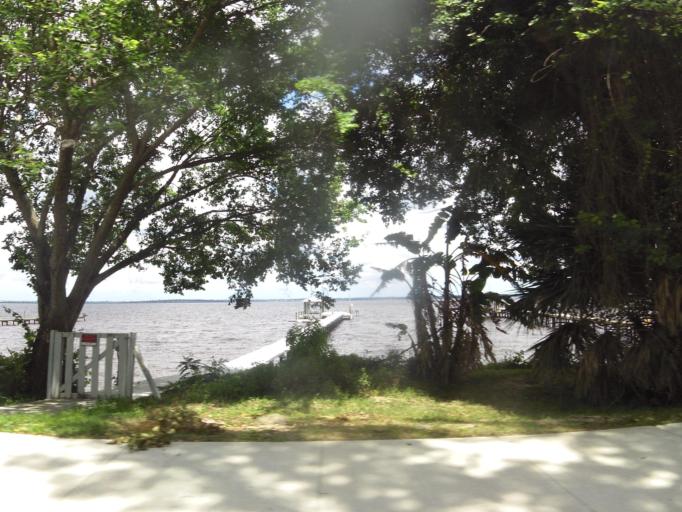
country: US
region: Florida
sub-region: Clay County
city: Orange Park
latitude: 30.1764
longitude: -81.6979
